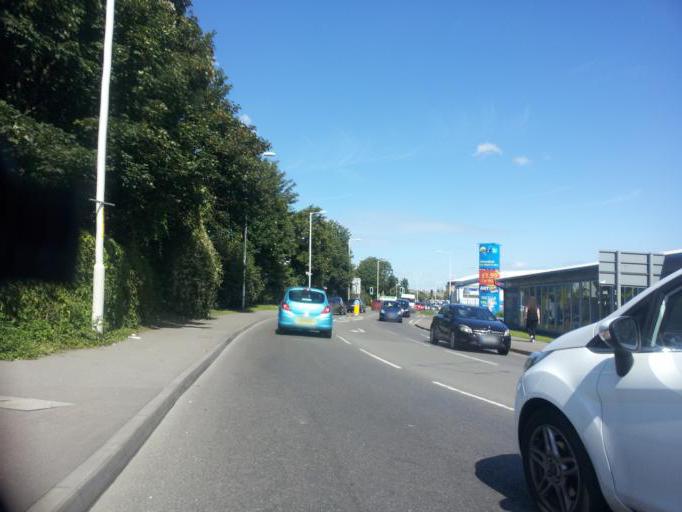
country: GB
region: England
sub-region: Kent
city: Sittingbourne
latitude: 51.3448
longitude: 0.7321
